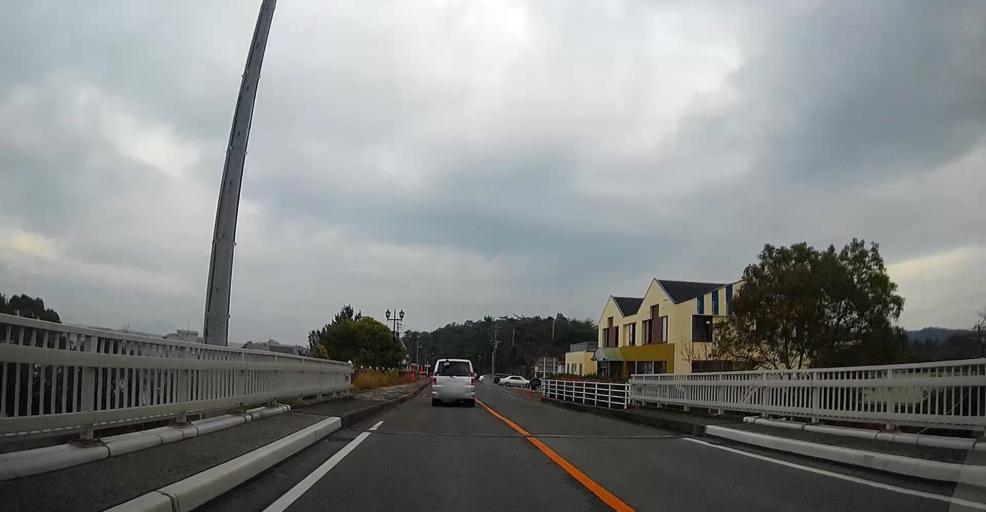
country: JP
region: Kumamoto
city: Yatsushiro
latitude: 32.5238
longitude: 130.4228
